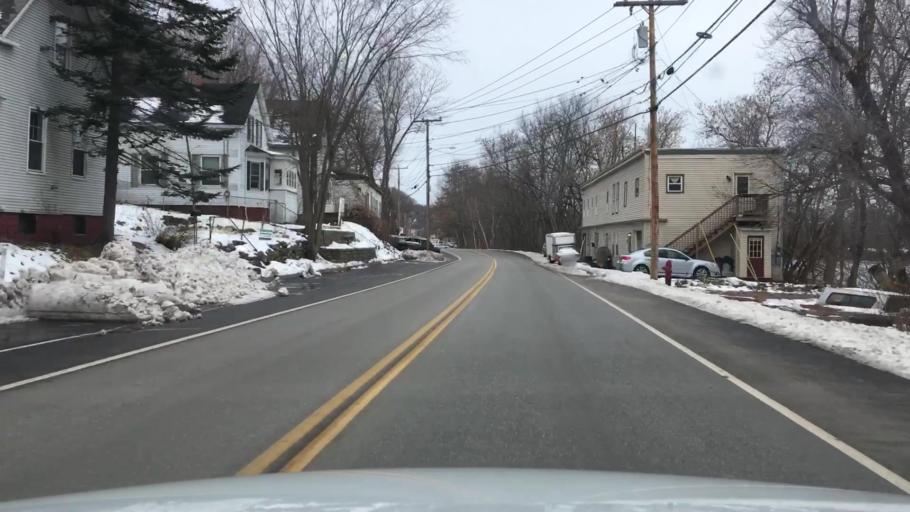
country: US
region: Maine
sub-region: Androscoggin County
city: Lewiston
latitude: 44.0837
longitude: -70.2142
